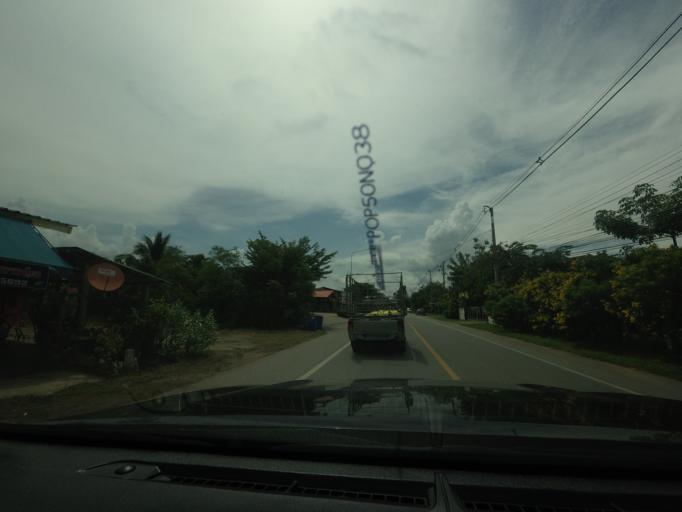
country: TH
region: Kanchanaburi
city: Phanom Thuan
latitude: 14.1052
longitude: 99.6551
